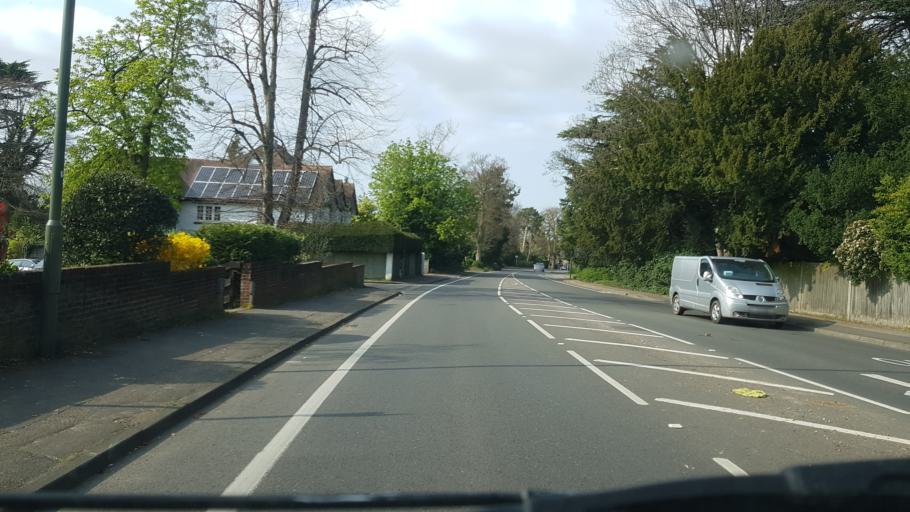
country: GB
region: England
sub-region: Surrey
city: Guildford
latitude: 51.2417
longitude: -0.5467
